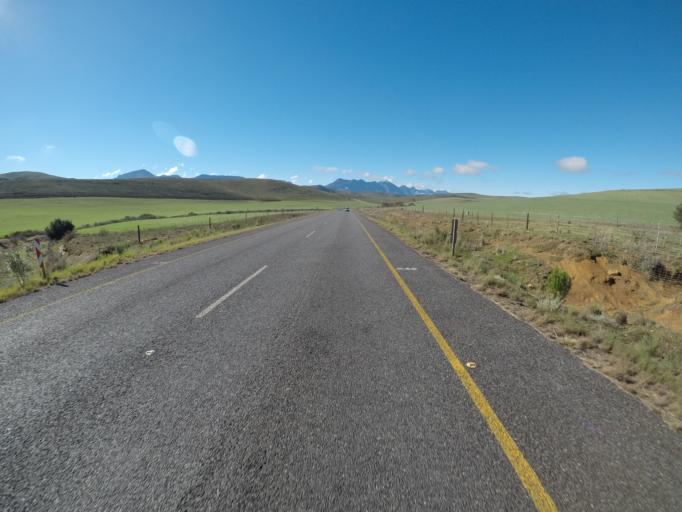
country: ZA
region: Western Cape
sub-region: Overberg District Municipality
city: Caledon
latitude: -34.0955
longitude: 19.5389
